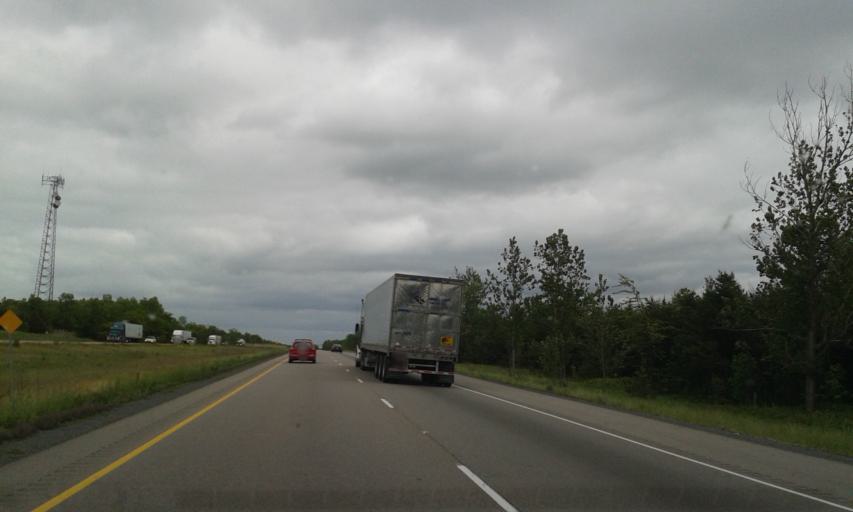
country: CA
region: Ontario
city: Skatepark
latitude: 44.2797
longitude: -76.7688
